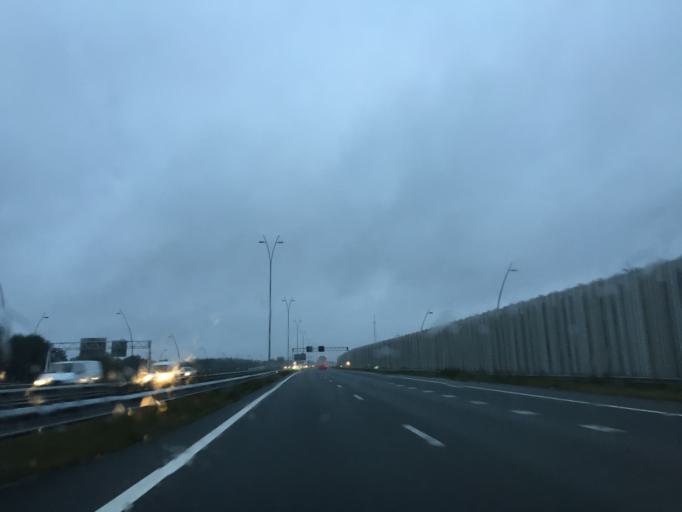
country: NL
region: North Brabant
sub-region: Gemeente Veldhoven
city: Veldhoven
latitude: 51.4115
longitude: 5.4302
